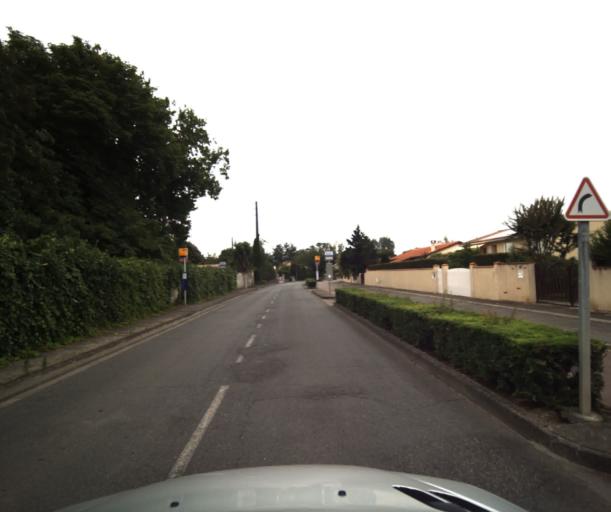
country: FR
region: Midi-Pyrenees
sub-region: Departement de la Haute-Garonne
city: Pinsaguel
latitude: 43.5150
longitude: 1.3929
